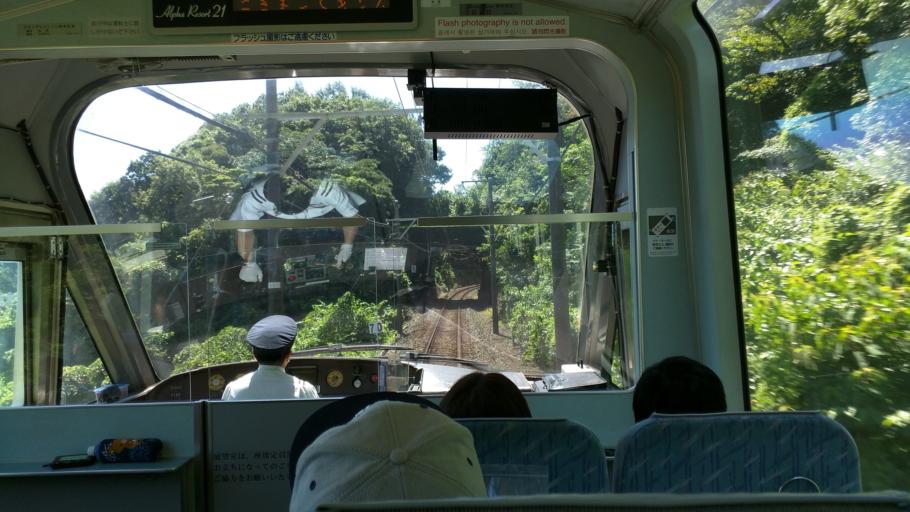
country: JP
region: Shizuoka
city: Ito
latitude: 34.9461
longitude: 139.1339
